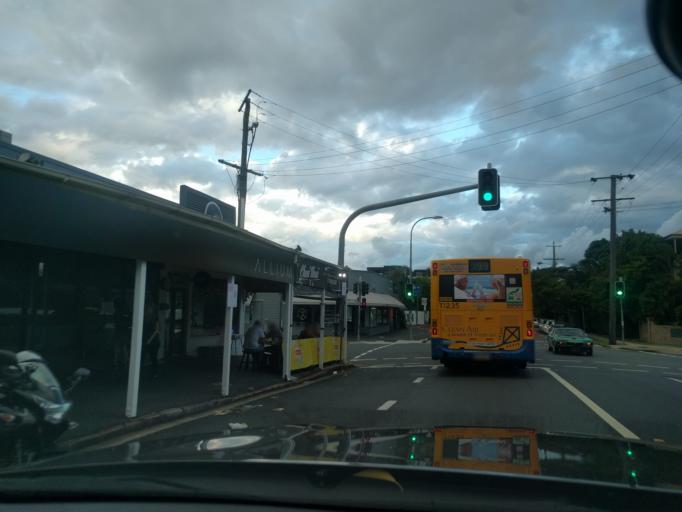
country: AU
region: Queensland
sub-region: Brisbane
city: Balmoral
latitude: -27.4642
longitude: 153.0490
